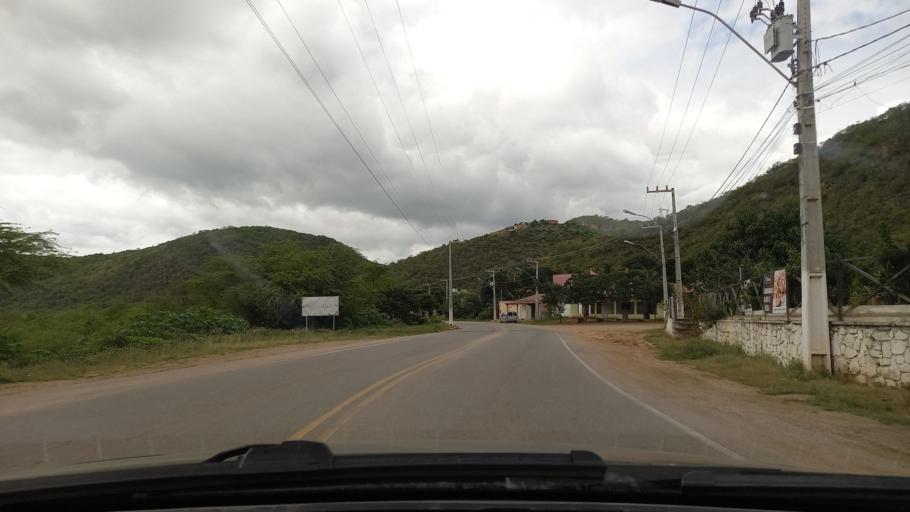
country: BR
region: Sergipe
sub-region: Caninde De Sao Francisco
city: Caninde de Sao Francisco
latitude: -9.6417
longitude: -37.7847
